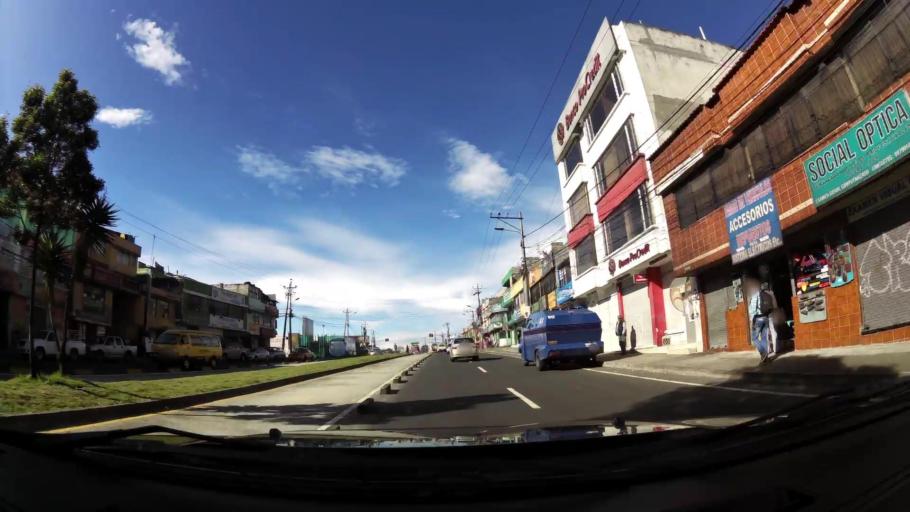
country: EC
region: Pichincha
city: Sangolqui
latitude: -0.3295
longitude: -78.5506
